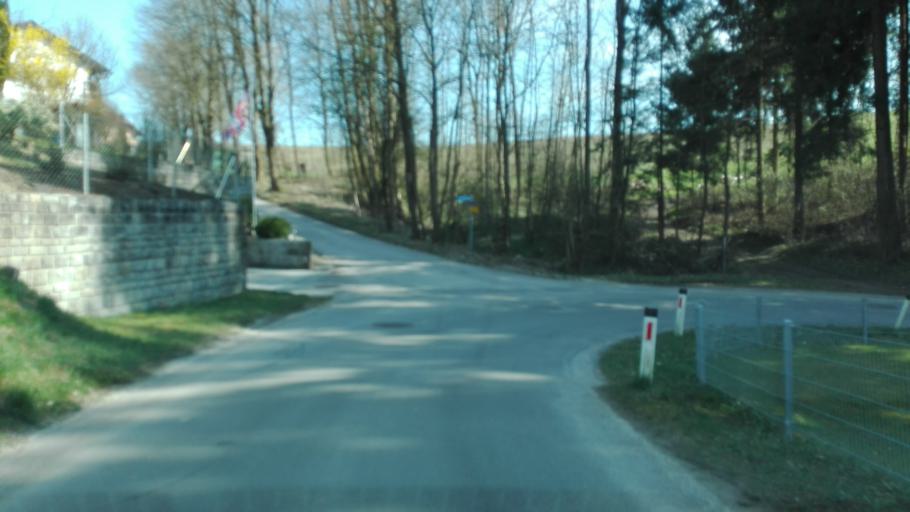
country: AT
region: Lower Austria
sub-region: Politischer Bezirk Amstetten
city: Ennsdorf
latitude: 48.2604
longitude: 14.5038
